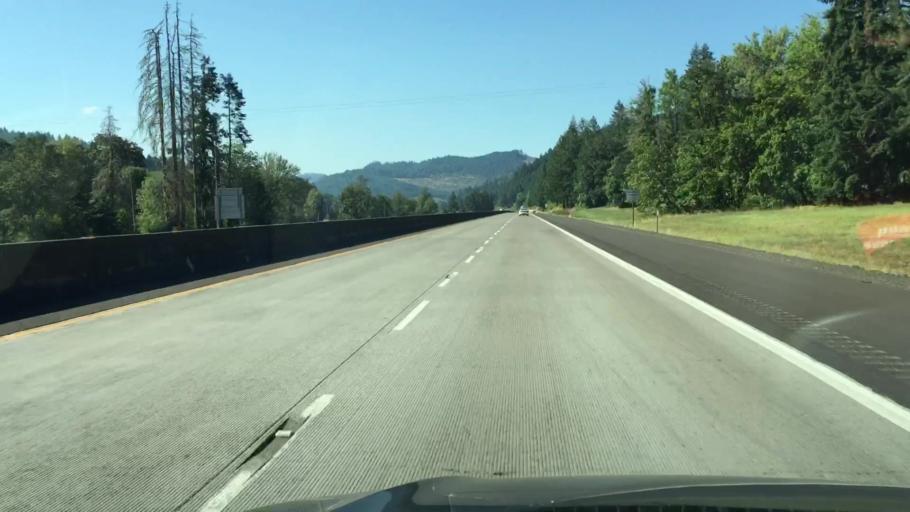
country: US
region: Oregon
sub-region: Douglas County
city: Yoncalla
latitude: 43.6571
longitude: -123.2061
